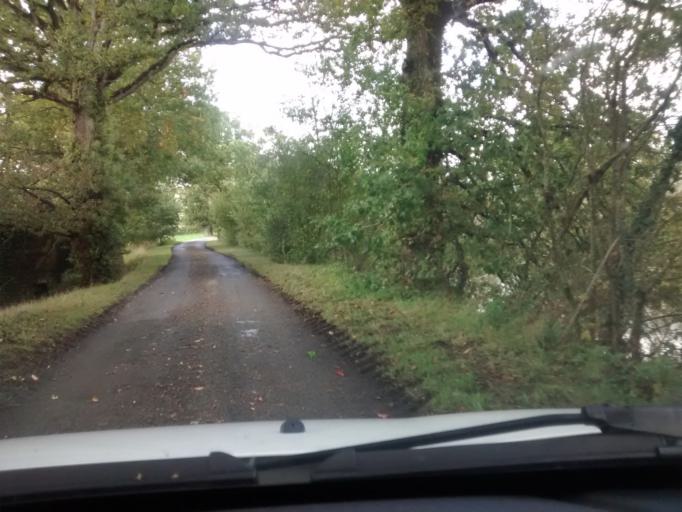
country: FR
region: Brittany
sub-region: Departement d'Ille-et-Vilaine
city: Chateaubourg
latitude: 48.1349
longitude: -1.4234
